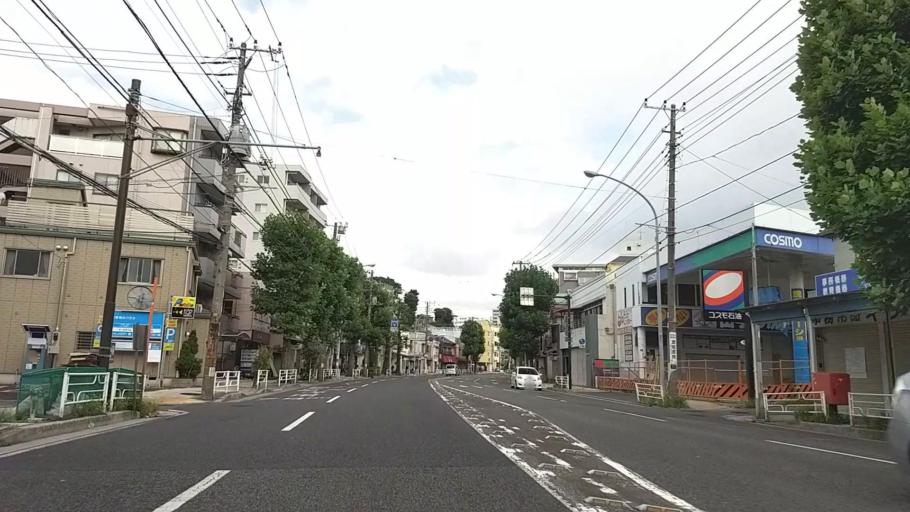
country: JP
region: Kanagawa
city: Yokohama
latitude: 35.4326
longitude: 139.6490
